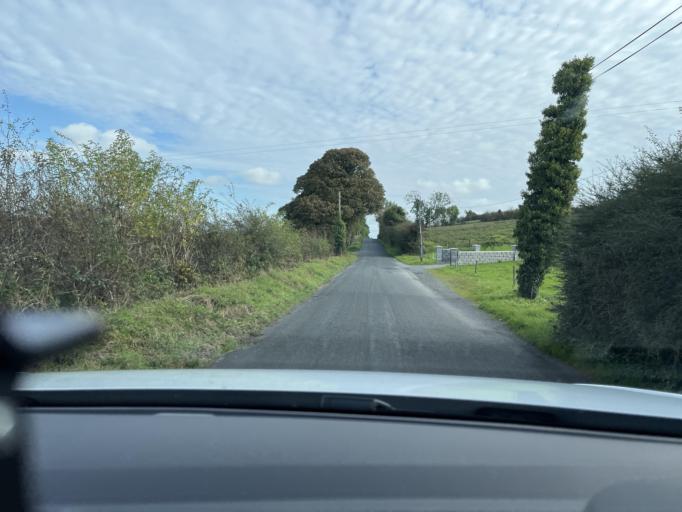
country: IE
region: Connaught
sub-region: Sligo
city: Ballymote
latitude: 54.0830
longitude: -8.4294
